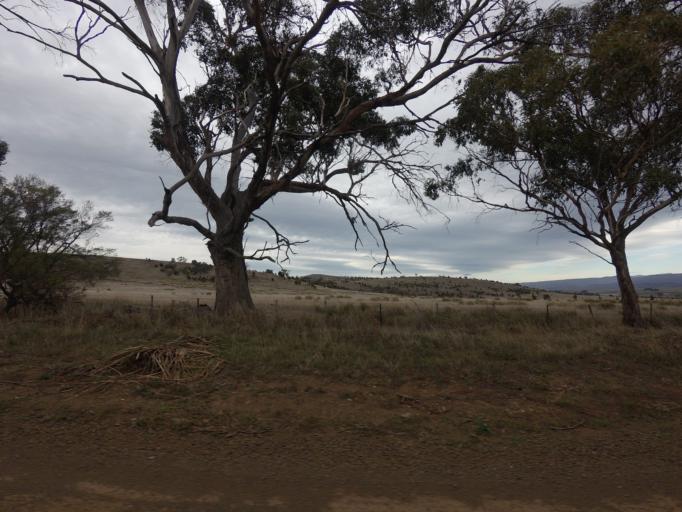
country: AU
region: Tasmania
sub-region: Derwent Valley
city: New Norfolk
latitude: -42.5534
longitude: 146.8944
